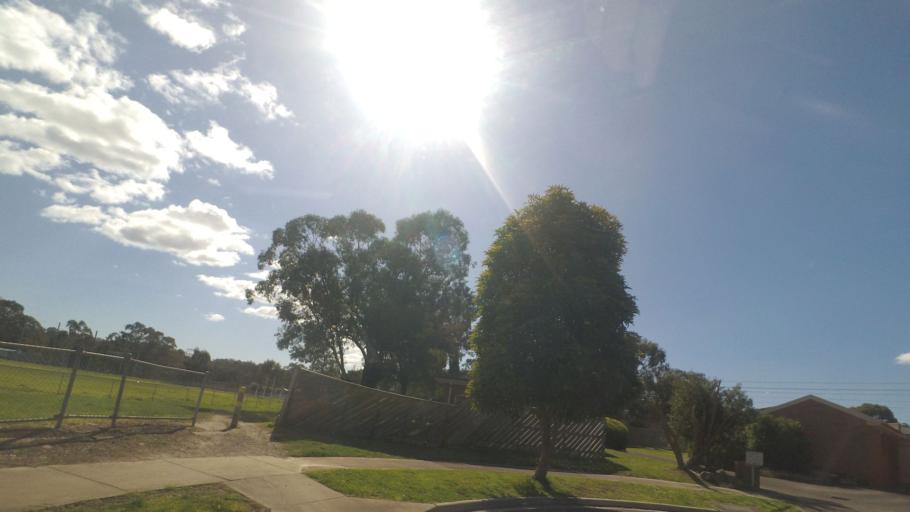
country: AU
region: Victoria
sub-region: Knox
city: Bayswater
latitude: -37.8375
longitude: 145.2633
